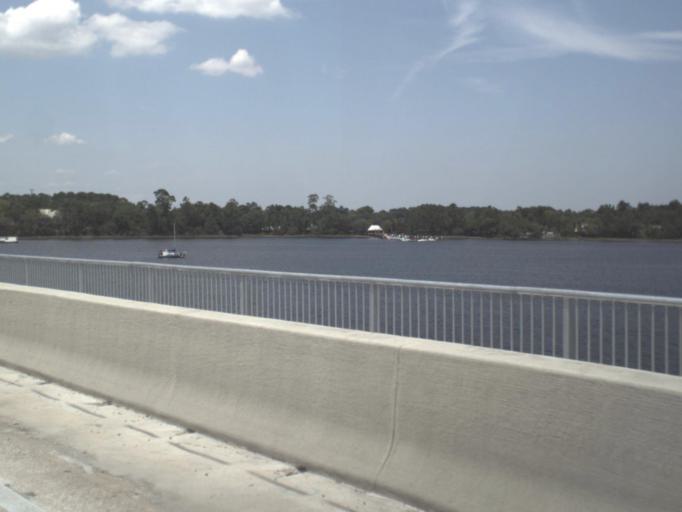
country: US
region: Florida
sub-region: Duval County
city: Jacksonville
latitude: 30.3939
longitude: -81.6477
